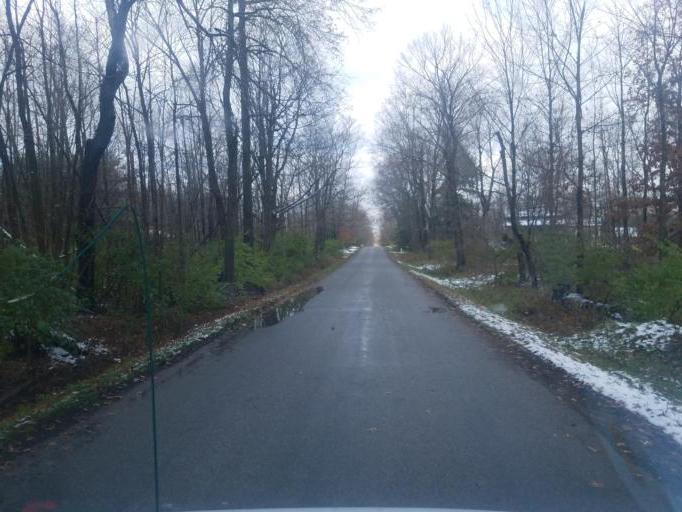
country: US
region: Ohio
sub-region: Morrow County
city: Mount Gilead
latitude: 40.4630
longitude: -82.8072
